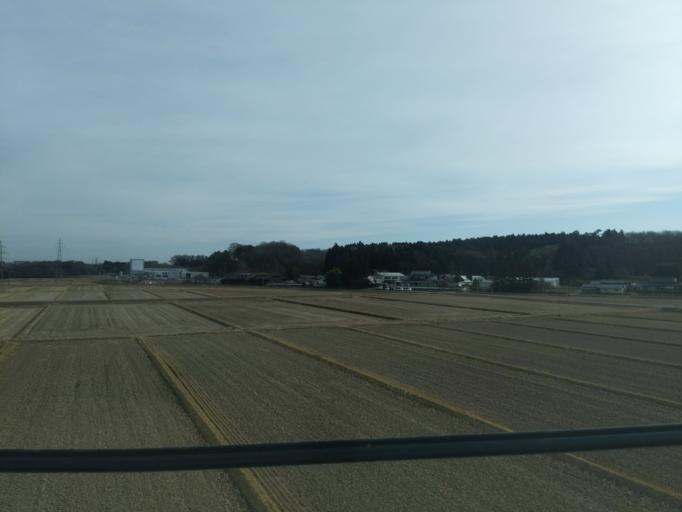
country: JP
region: Iwate
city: Ichinoseki
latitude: 38.7396
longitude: 141.0665
